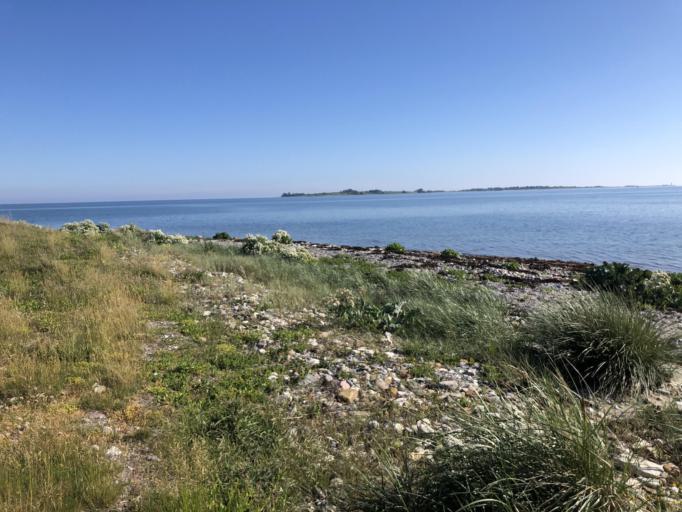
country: DK
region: Zealand
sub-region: Slagelse Kommune
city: Skaelskor
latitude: 55.1988
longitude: 11.1746
